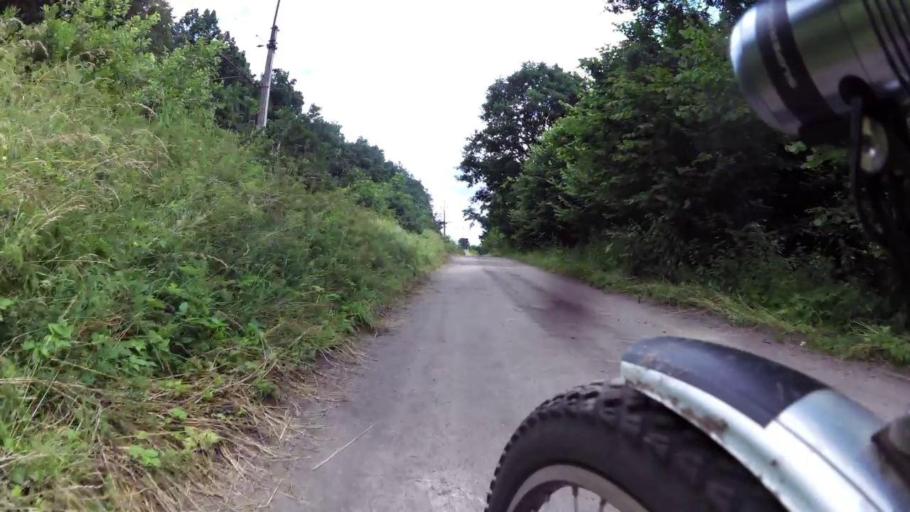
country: PL
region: West Pomeranian Voivodeship
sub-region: Powiat swidwinski
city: Rabino
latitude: 53.8646
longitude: 15.9452
